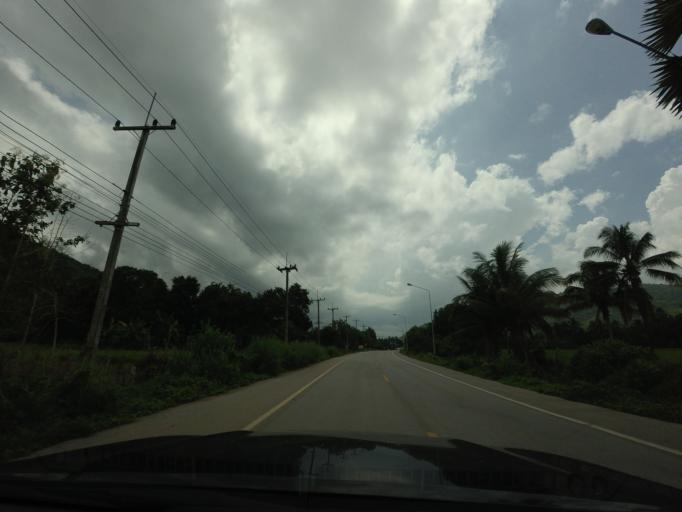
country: TH
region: Loei
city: Pak Chom
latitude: 18.0220
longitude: 101.7638
